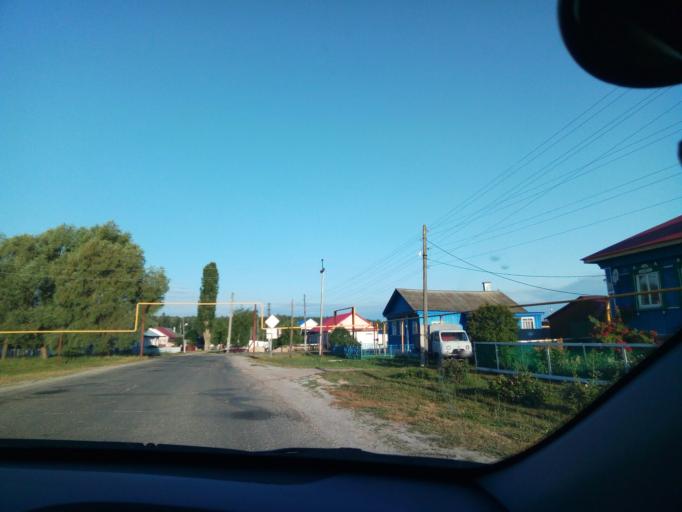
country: RU
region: Nizjnij Novgorod
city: Voznesenskoye
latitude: 54.8866
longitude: 42.7741
